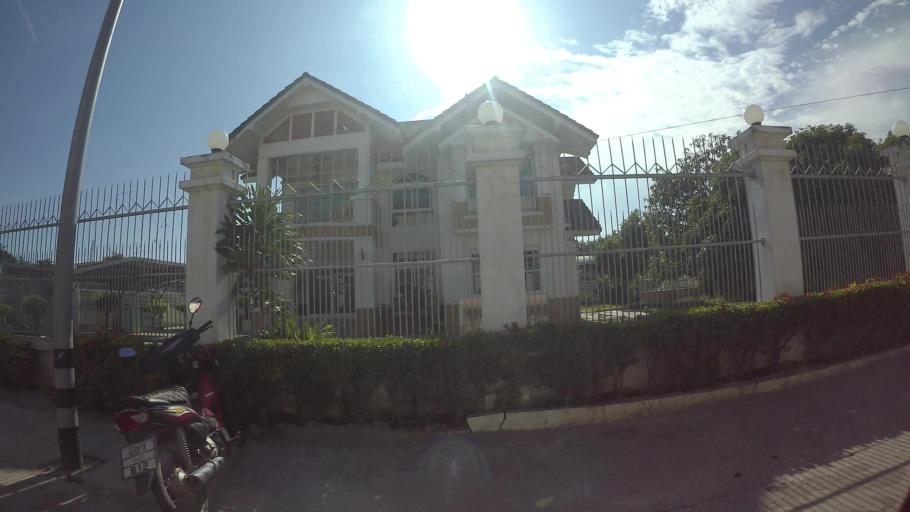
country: TH
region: Rayong
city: Rayong
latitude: 12.6677
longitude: 101.2988
